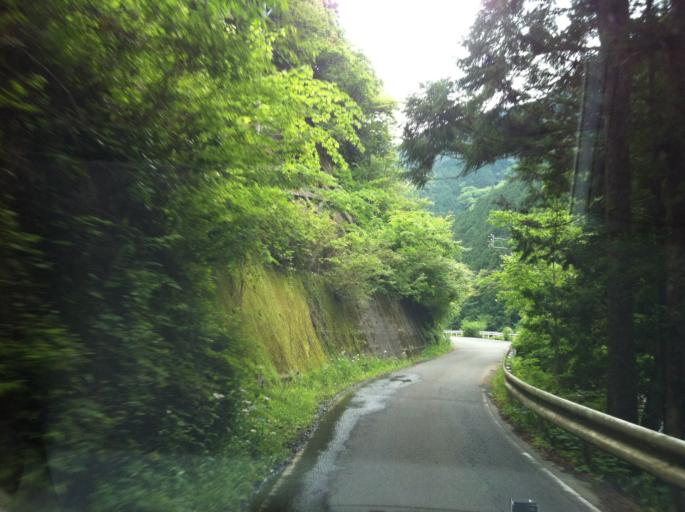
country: JP
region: Shizuoka
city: Shizuoka-shi
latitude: 35.1695
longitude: 138.3140
